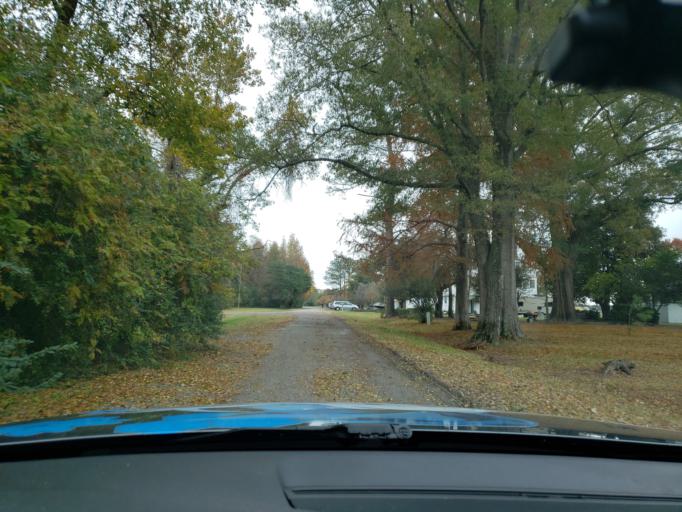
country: US
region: Virginia
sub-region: City of Chesapeake
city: Chesapeake
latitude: 36.7089
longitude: -76.1288
